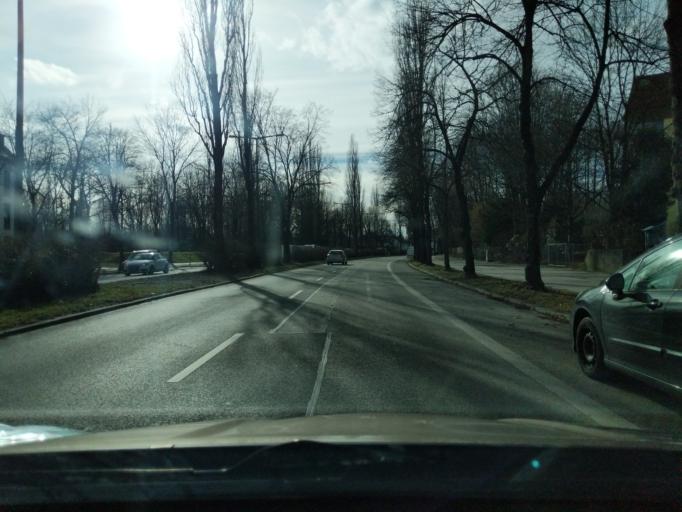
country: DE
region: Bavaria
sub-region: Upper Bavaria
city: Bogenhausen
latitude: 48.1544
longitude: 11.6357
